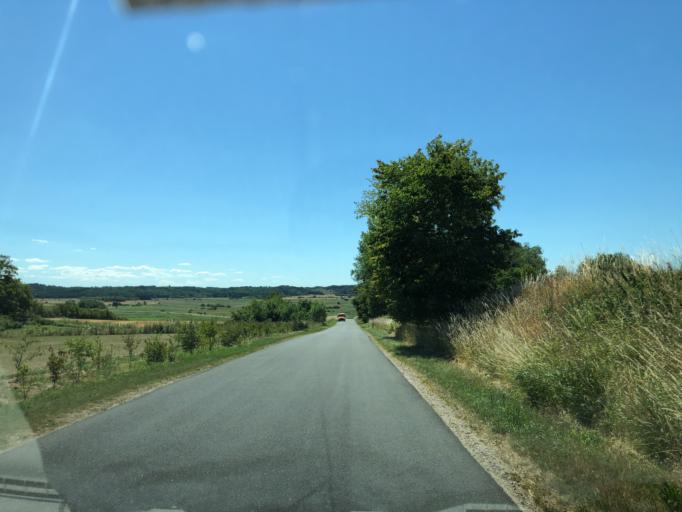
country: DK
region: Central Jutland
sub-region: Viborg Kommune
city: Viborg
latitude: 56.5560
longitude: 9.4249
